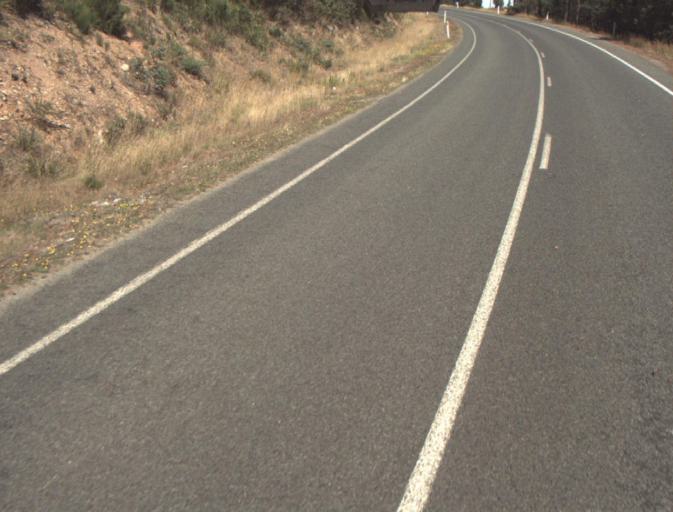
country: AU
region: Tasmania
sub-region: Dorset
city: Scottsdale
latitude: -41.3190
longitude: 147.3643
